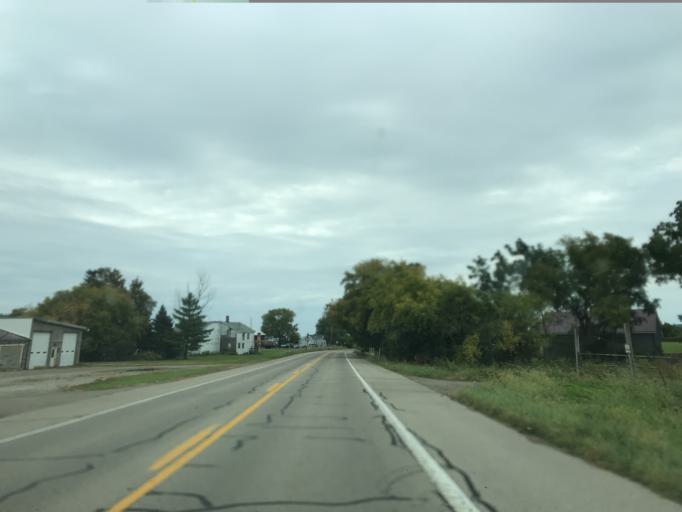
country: US
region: Pennsylvania
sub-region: Erie County
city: North East
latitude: 42.2413
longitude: -79.7650
